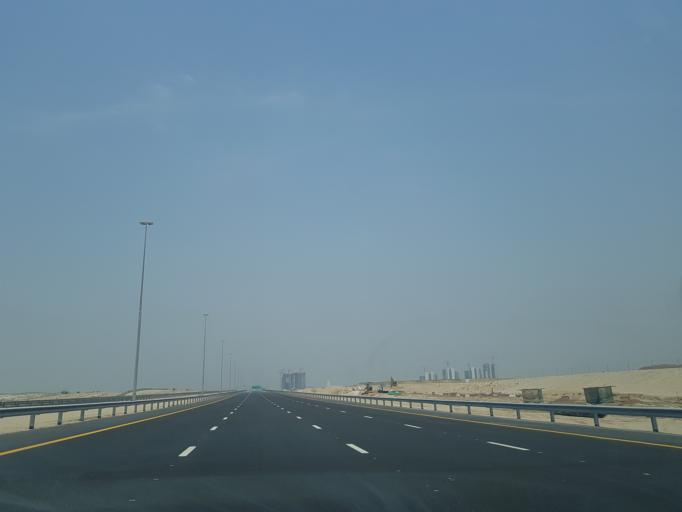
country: AE
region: Dubai
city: Dubai
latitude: 25.0162
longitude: 55.2256
